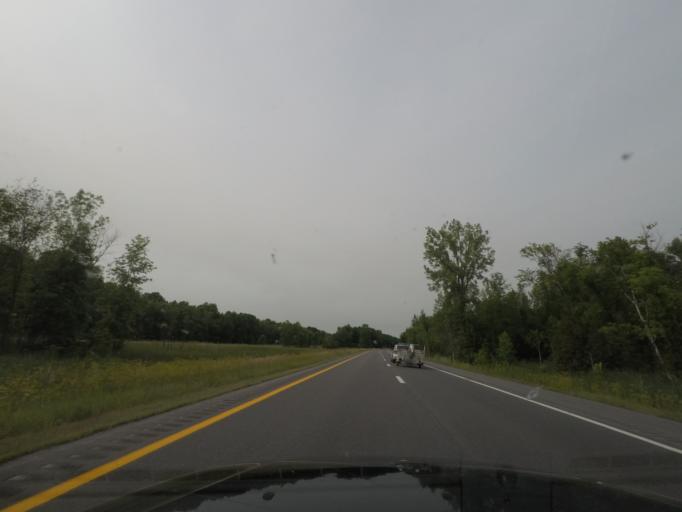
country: US
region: New York
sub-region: Clinton County
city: Champlain
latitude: 44.8504
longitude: -73.4484
